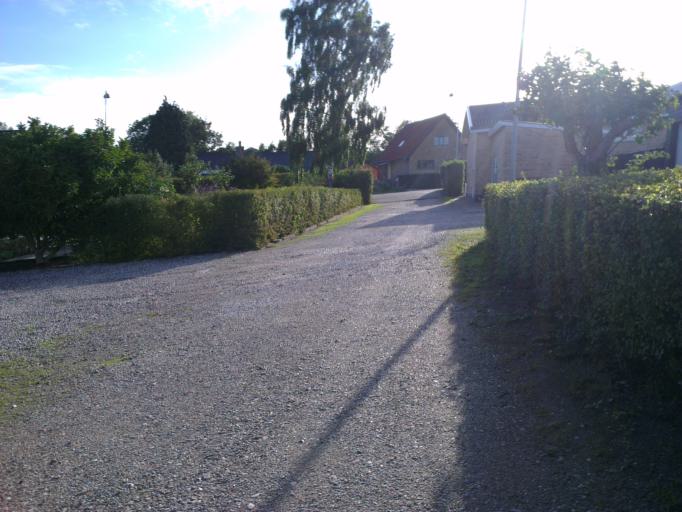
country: DK
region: Capital Region
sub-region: Frederikssund Kommune
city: Frederikssund
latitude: 55.8498
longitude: 12.0631
